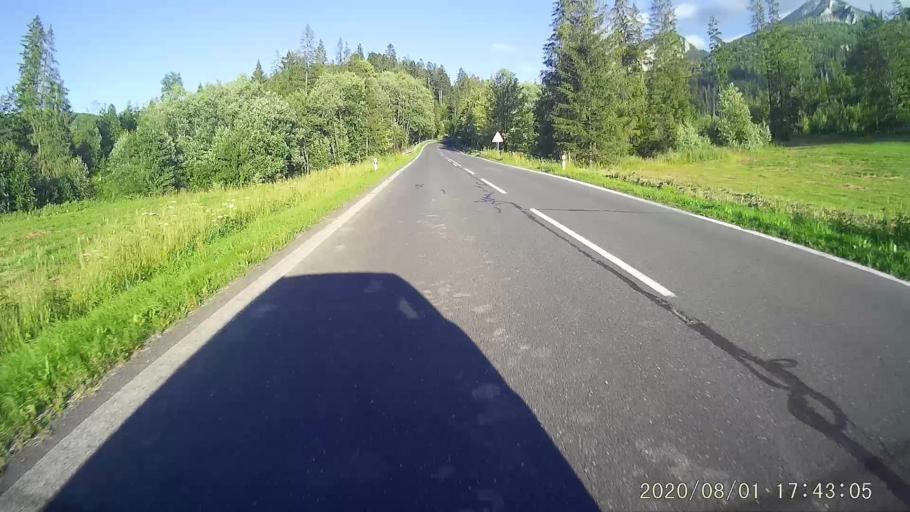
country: SK
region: Presovsky
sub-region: Okres Poprad
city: Zdiar
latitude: 49.2775
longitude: 20.1813
